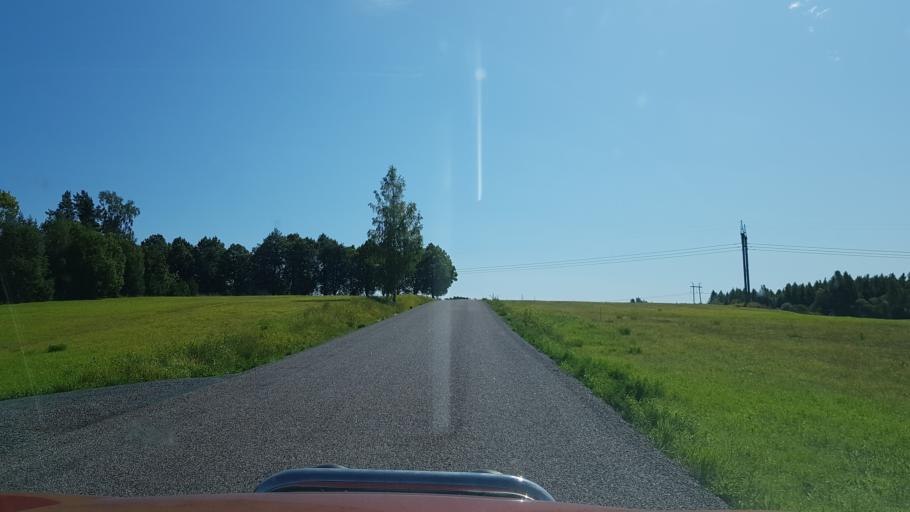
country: EE
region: Tartu
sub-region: Elva linn
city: Elva
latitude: 58.2464
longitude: 26.3823
